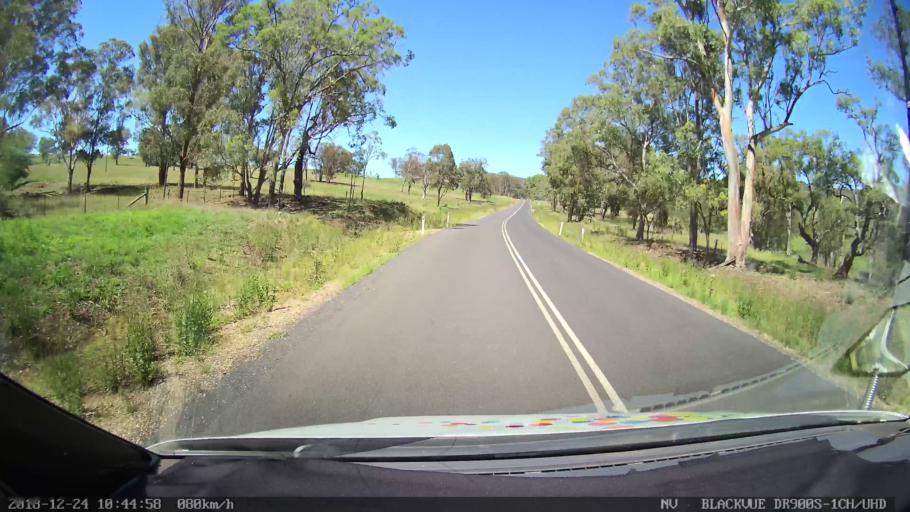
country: AU
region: New South Wales
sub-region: Upper Hunter Shire
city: Merriwa
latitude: -31.8983
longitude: 150.4398
